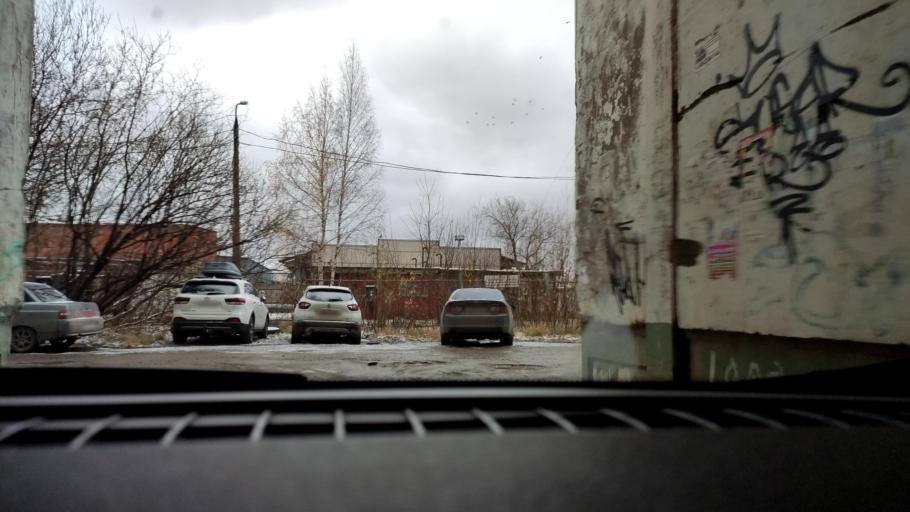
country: RU
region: Perm
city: Perm
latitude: 57.9726
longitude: 56.1999
